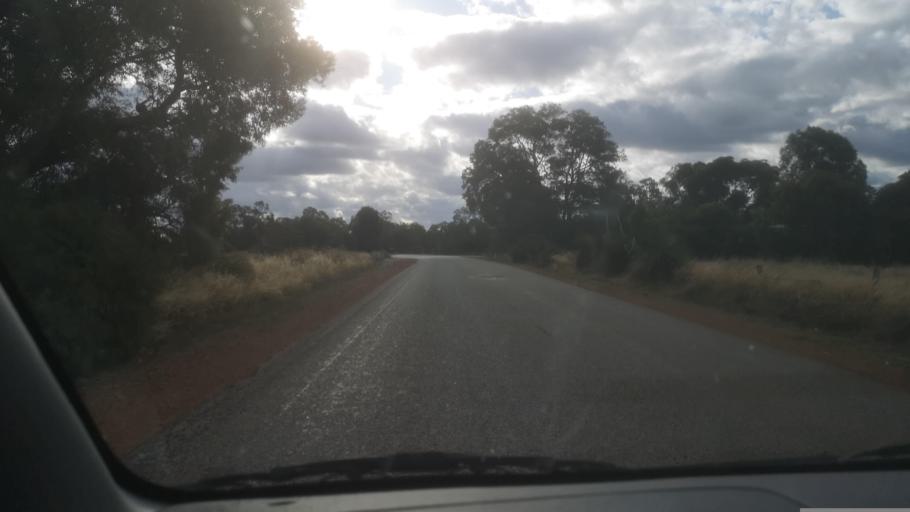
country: AU
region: Western Australia
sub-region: Chittering
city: Lower Chittering
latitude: -31.3274
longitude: 116.0286
